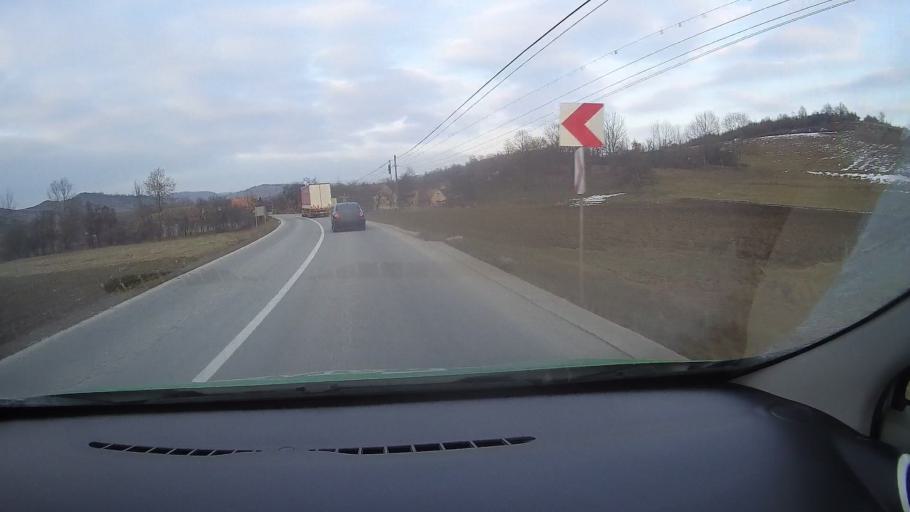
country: RO
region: Harghita
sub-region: Comuna Simonesti
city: Simonesti
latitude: 46.3445
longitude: 25.1181
